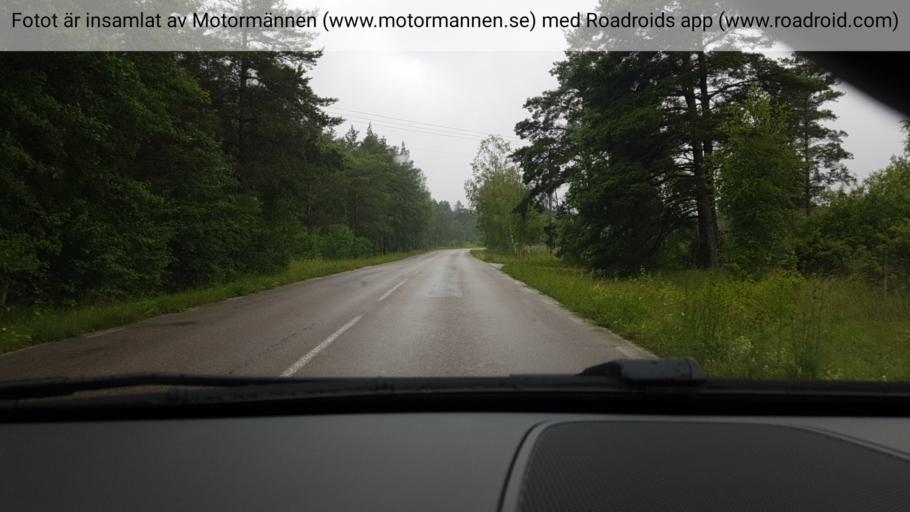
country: SE
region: Gotland
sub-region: Gotland
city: Slite
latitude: 57.8278
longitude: 18.8006
